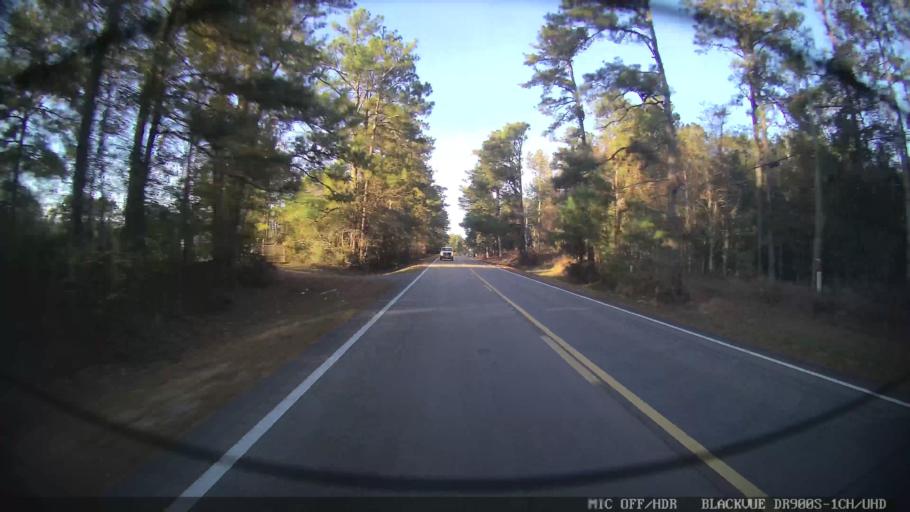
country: US
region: Mississippi
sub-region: Lamar County
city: Lumberton
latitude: 31.0177
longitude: -89.4505
